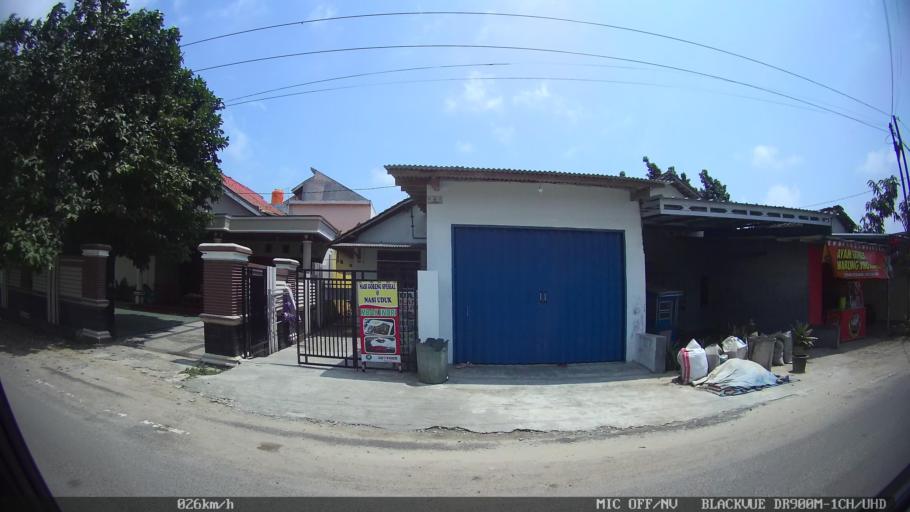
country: ID
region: Lampung
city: Kedaton
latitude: -5.3695
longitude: 105.2709
